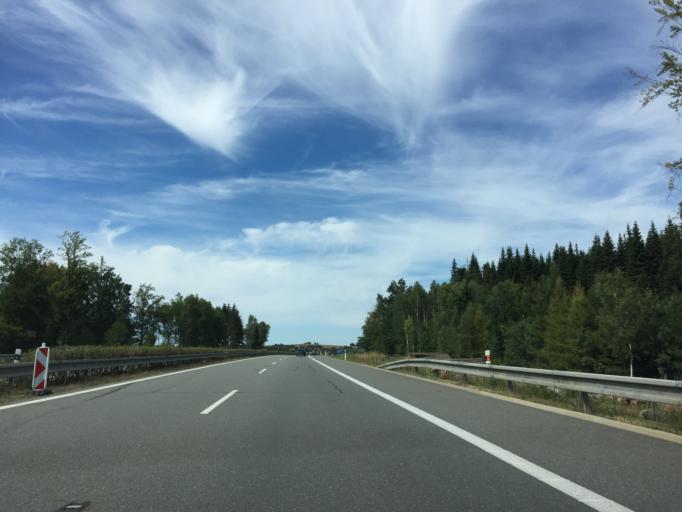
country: CZ
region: Jihocesky
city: Chotoviny
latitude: 49.5251
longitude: 14.6681
